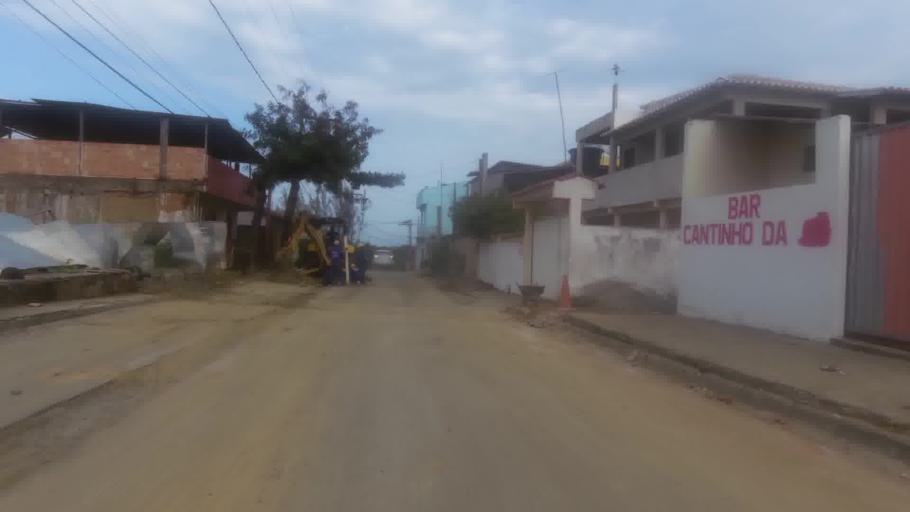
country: BR
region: Espirito Santo
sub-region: Guarapari
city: Guarapari
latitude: -20.7680
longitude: -40.5748
